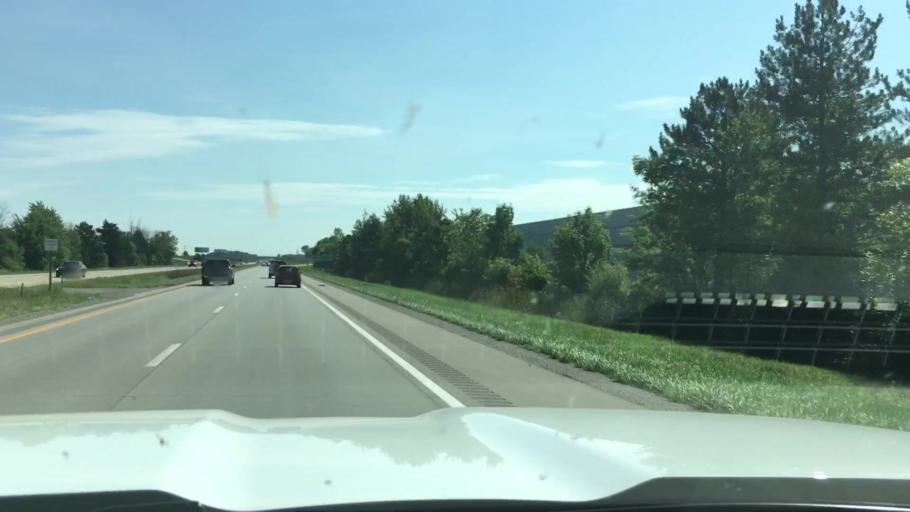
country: US
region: Michigan
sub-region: Bay County
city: Auburn
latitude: 43.5960
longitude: -84.0017
